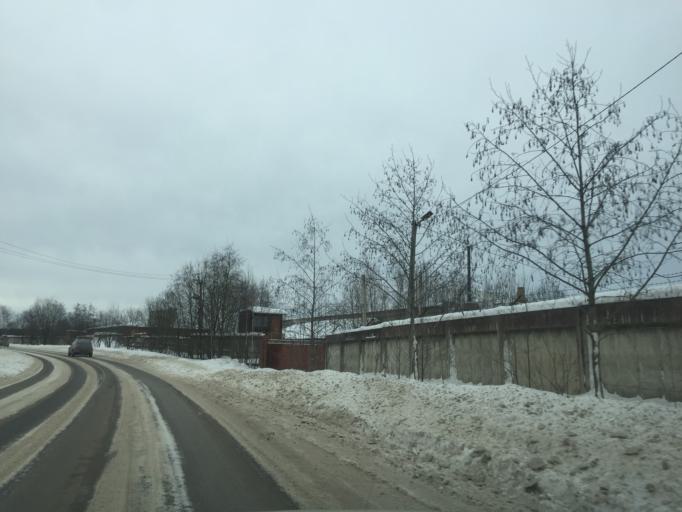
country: RU
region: Leningrad
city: Imeni Sverdlova
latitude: 59.7897
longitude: 30.6980
